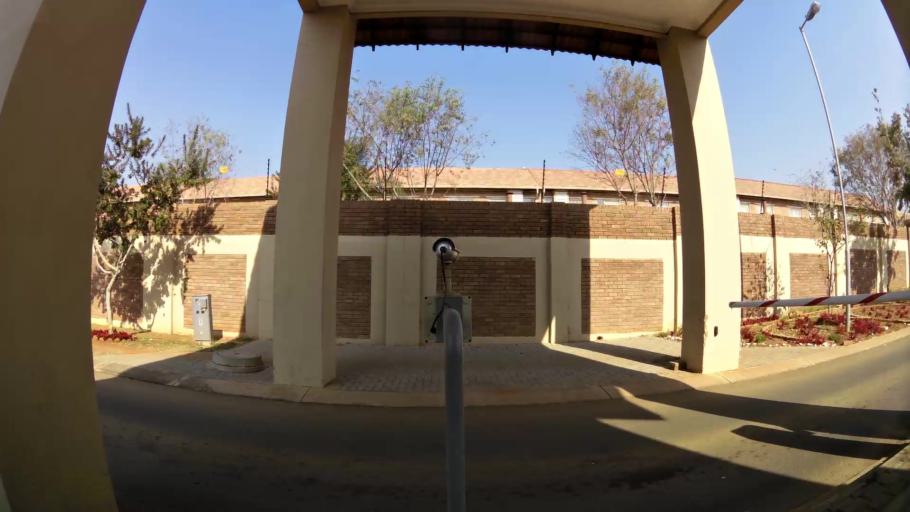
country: ZA
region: Gauteng
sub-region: City of Tshwane Metropolitan Municipality
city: Pretoria
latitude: -25.7805
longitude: 28.3496
